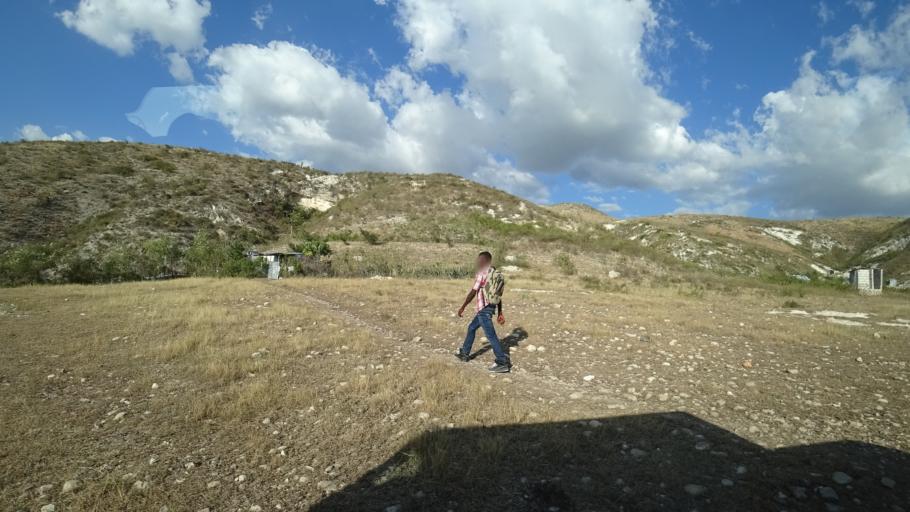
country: HT
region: Ouest
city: Cabaret
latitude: 18.6912
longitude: -72.3104
